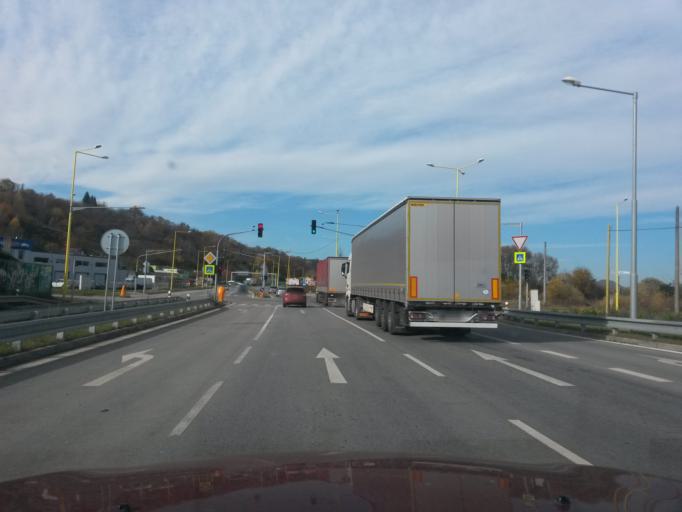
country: SK
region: Presovsky
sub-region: Okres Presov
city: Presov
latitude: 48.9828
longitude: 21.2355
